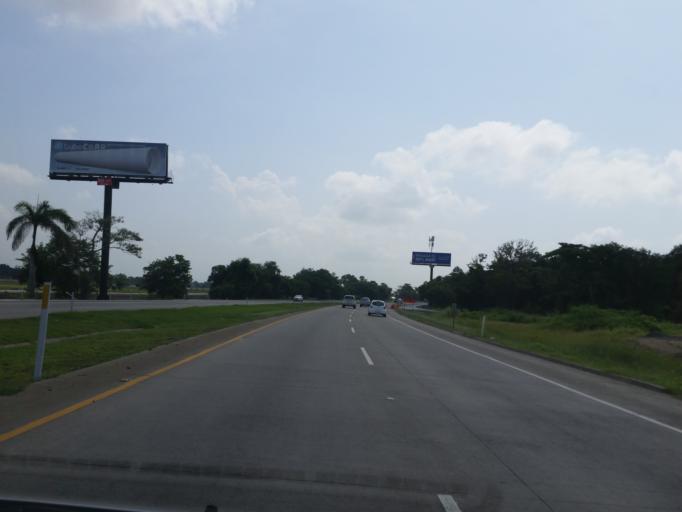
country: PA
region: Panama
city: San Miguelito
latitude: 9.0338
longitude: -79.4408
